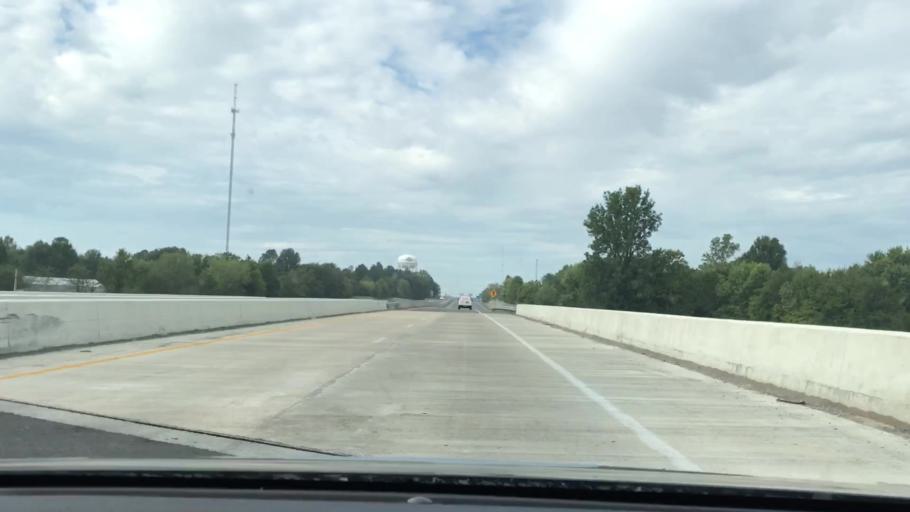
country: US
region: Kentucky
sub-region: Graves County
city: Mayfield
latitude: 36.7675
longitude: -88.6429
